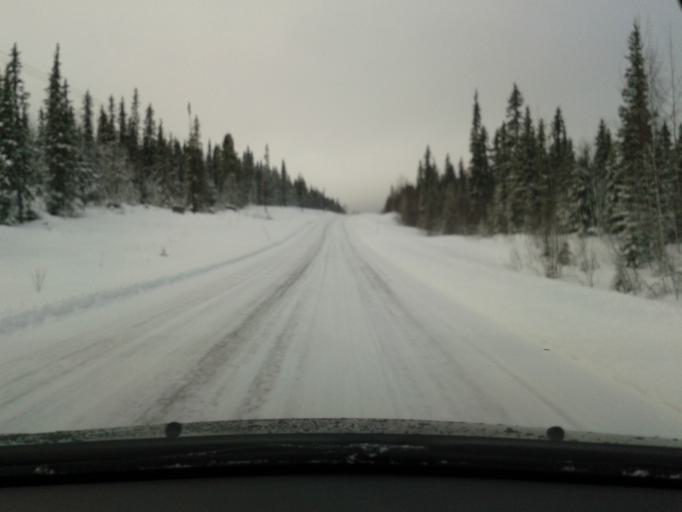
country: SE
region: Vaesterbotten
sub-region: Vilhelmina Kommun
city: Sjoberg
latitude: 65.2086
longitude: 16.0067
